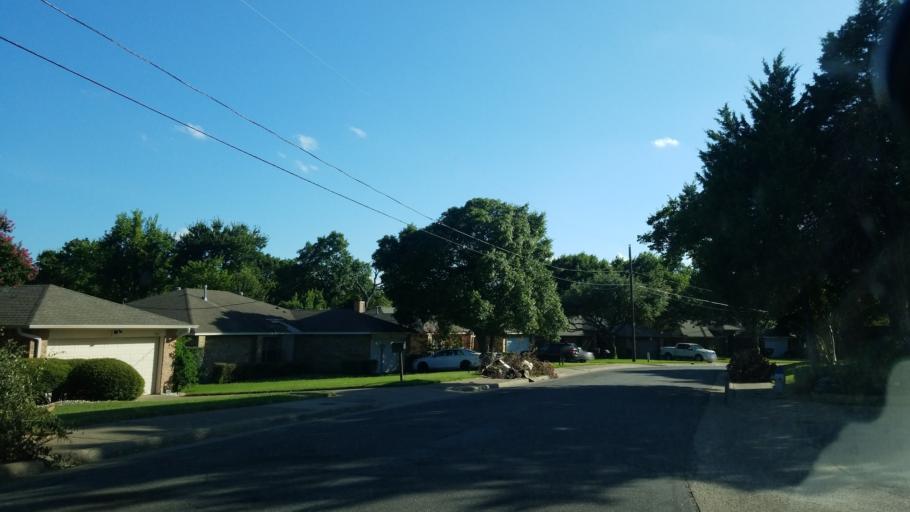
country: US
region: Texas
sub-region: Dallas County
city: Balch Springs
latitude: 32.7809
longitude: -96.7018
